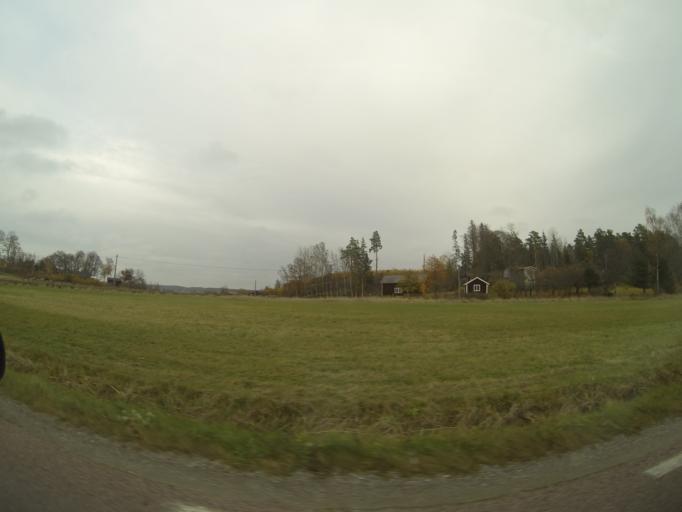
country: SE
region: Vaestmanland
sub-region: Vasteras
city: Skultuna
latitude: 59.6479
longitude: 16.4659
